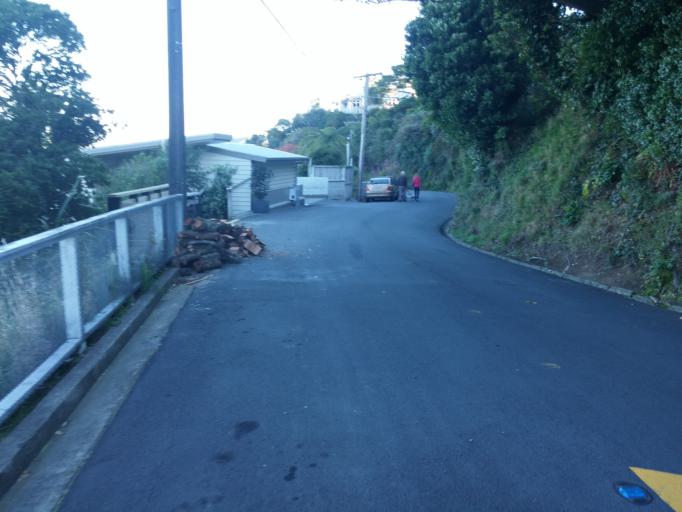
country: NZ
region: Wellington
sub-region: Wellington City
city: Kelburn
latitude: -41.2812
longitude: 174.7605
